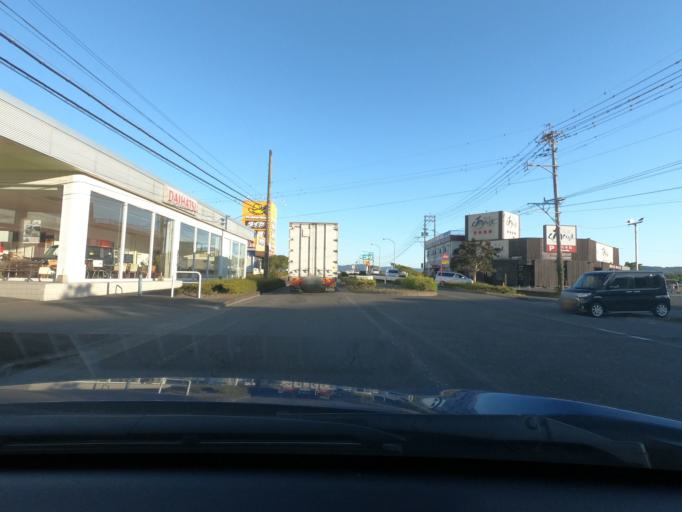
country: JP
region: Kagoshima
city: Satsumasendai
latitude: 31.8377
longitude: 130.2854
